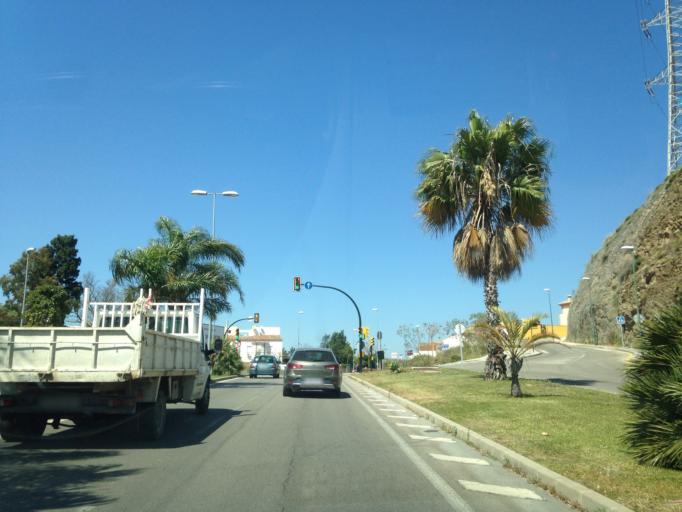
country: ES
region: Andalusia
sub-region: Provincia de Malaga
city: Malaga
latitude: 36.7331
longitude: -4.4760
